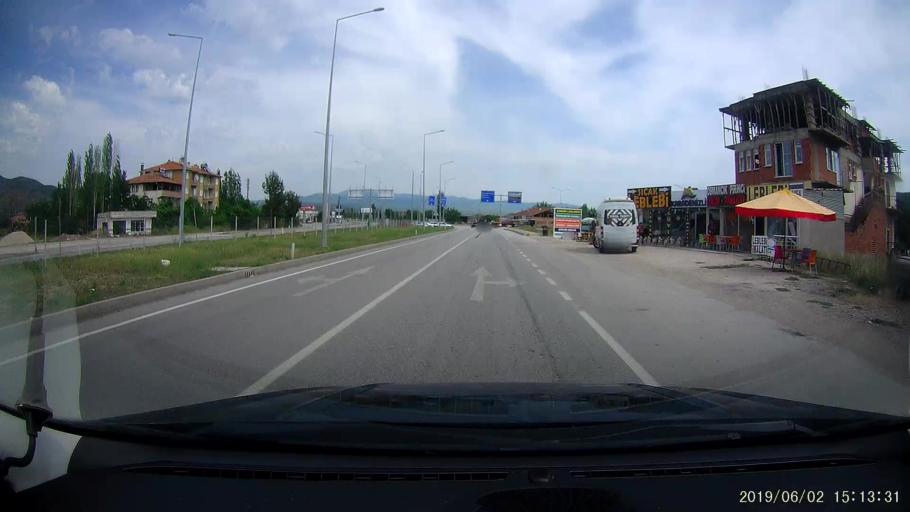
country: TR
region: Corum
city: Osmancik
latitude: 40.9719
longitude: 34.8222
